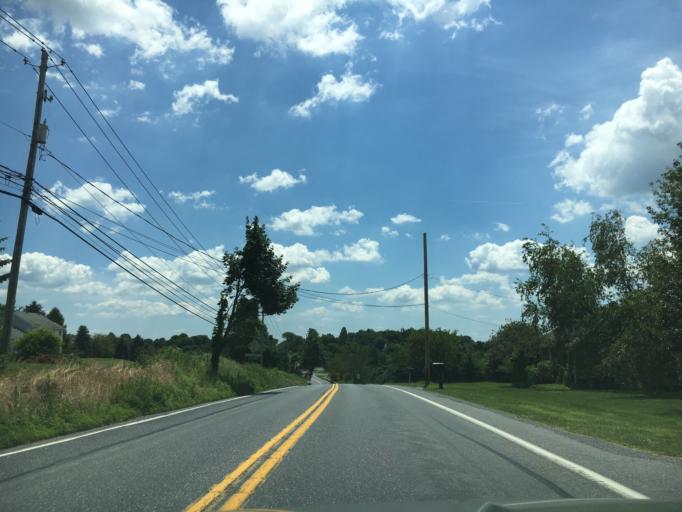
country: US
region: Pennsylvania
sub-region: Lehigh County
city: Schnecksville
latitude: 40.6881
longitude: -75.5871
